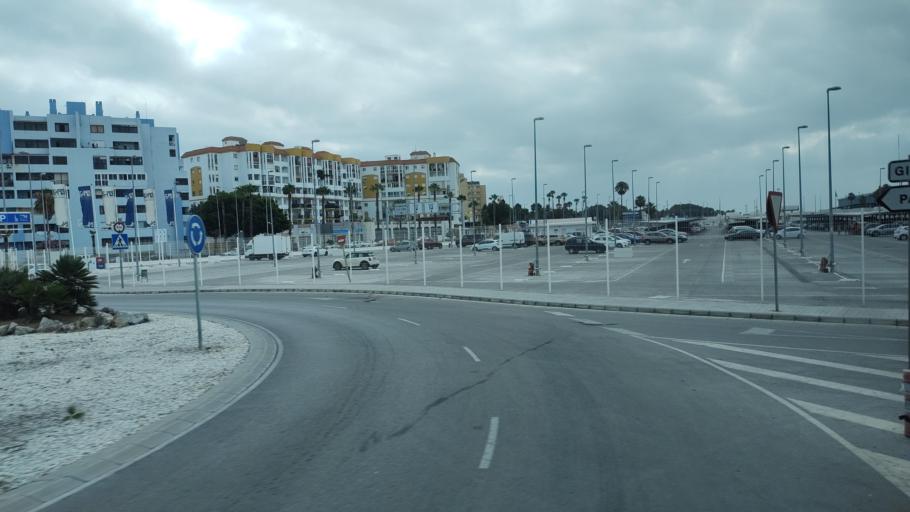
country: GI
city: Gibraltar
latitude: 36.1555
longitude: -5.3521
